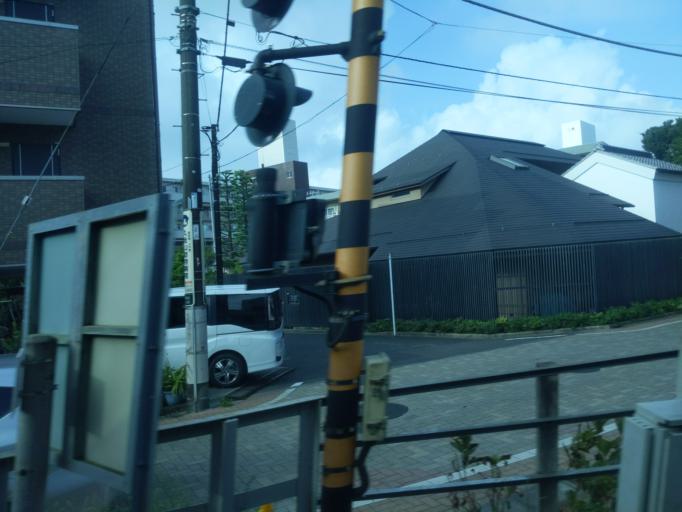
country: JP
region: Tokyo
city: Mitaka-shi
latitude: 35.6887
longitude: 139.5986
